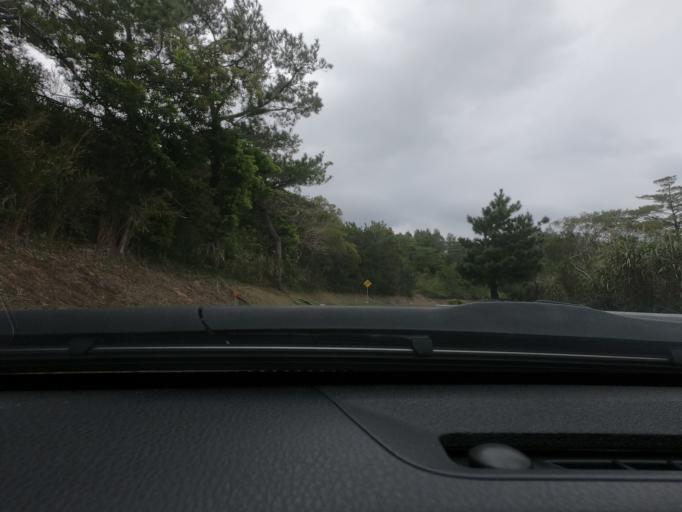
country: JP
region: Okinawa
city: Ishikawa
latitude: 26.4586
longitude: 127.9006
